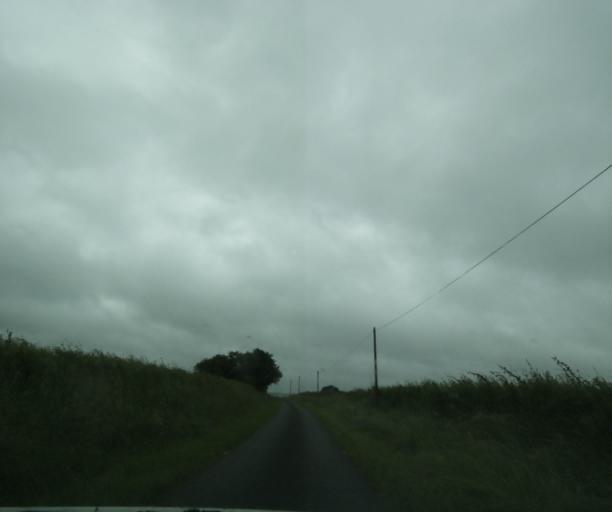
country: FR
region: Bourgogne
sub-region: Departement de Saone-et-Loire
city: Genelard
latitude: 46.5618
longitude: 4.2413
